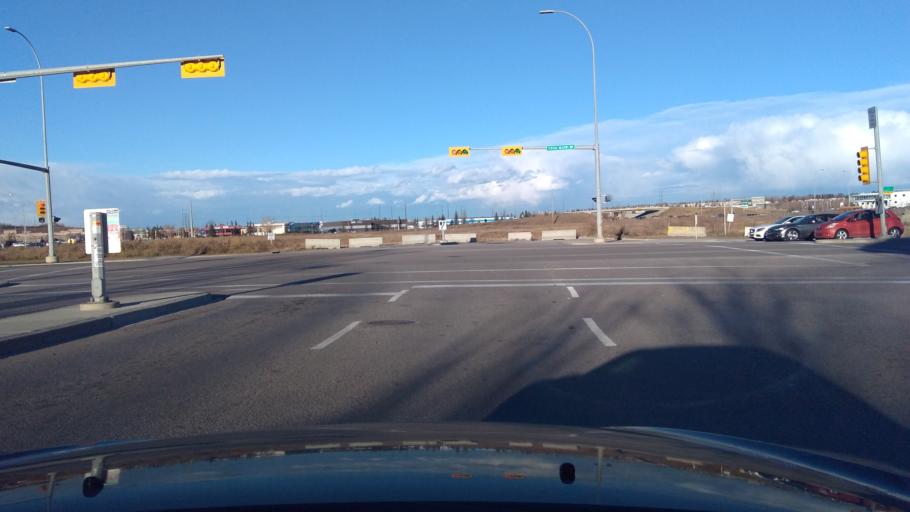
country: CA
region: Alberta
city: Calgary
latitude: 50.9832
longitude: -114.0401
